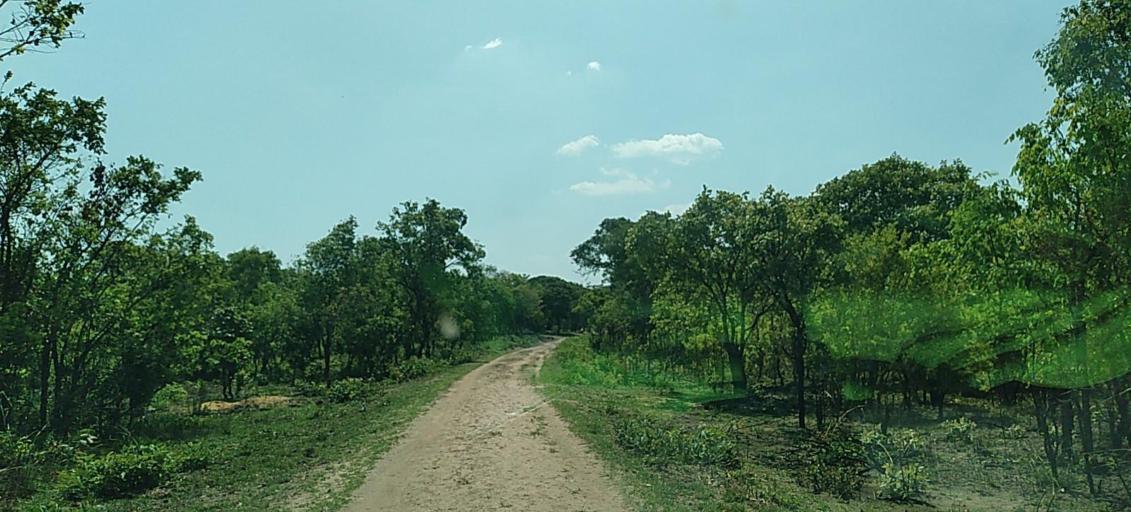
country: CD
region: Katanga
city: Kolwezi
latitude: -11.2763
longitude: 25.1115
